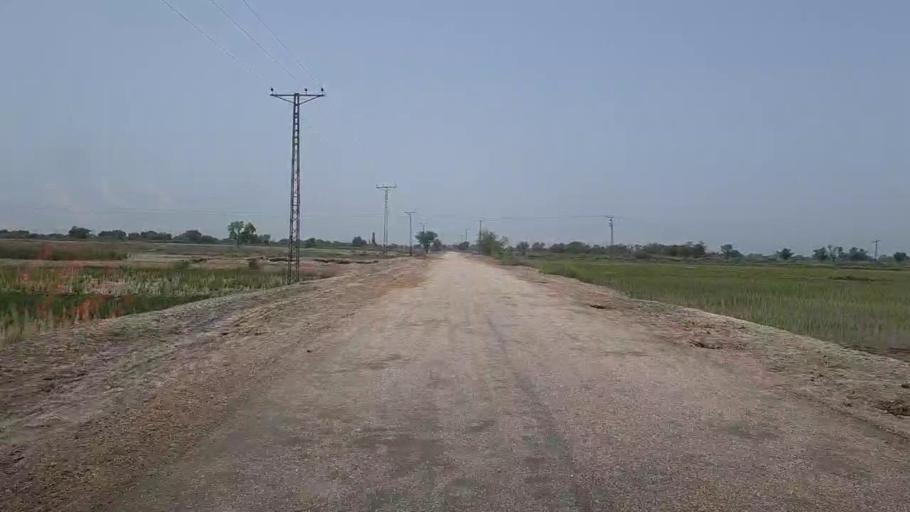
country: PK
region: Sindh
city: Pad Idan
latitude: 26.8343
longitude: 68.3207
